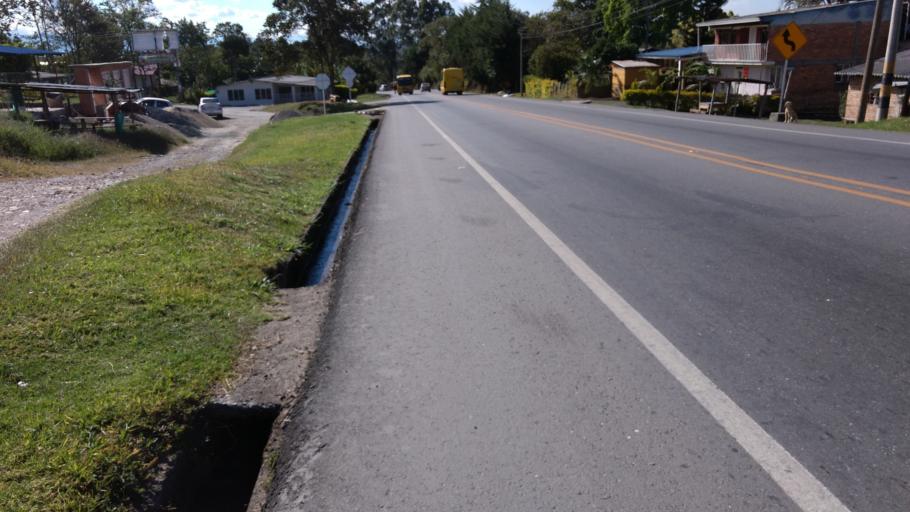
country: CO
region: Cauca
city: Cajibio
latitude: 2.5271
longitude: -76.5533
